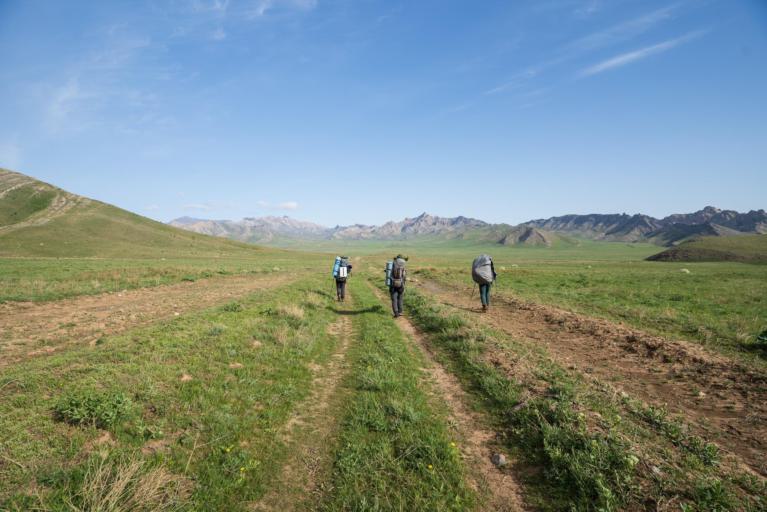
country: KZ
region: Ongtustik Qazaqstan
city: Ashchysay
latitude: 43.6943
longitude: 68.8619
